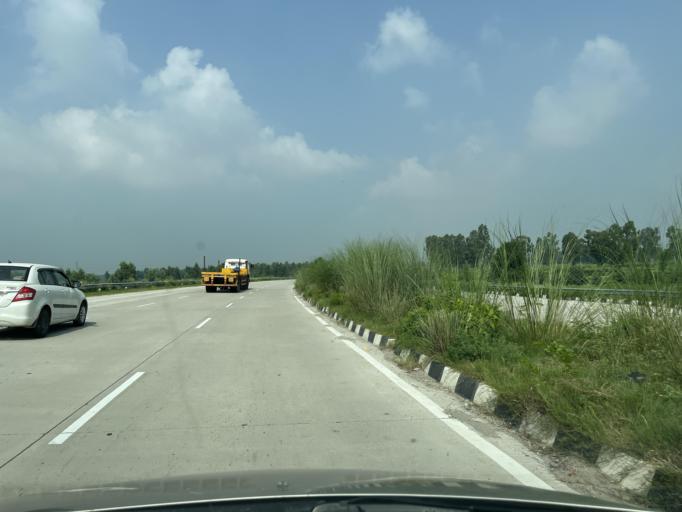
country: IN
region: Uttarakhand
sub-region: Udham Singh Nagar
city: Kashipur
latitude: 29.1634
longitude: 78.9632
